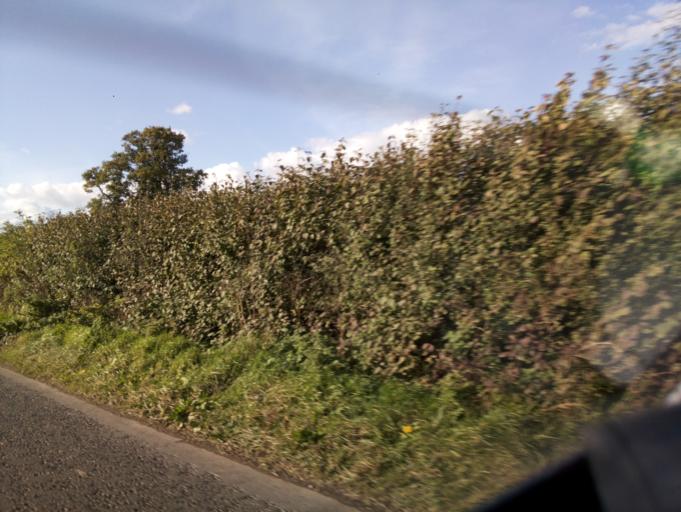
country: GB
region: England
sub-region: Herefordshire
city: Clifford
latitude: 52.1183
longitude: -3.0628
